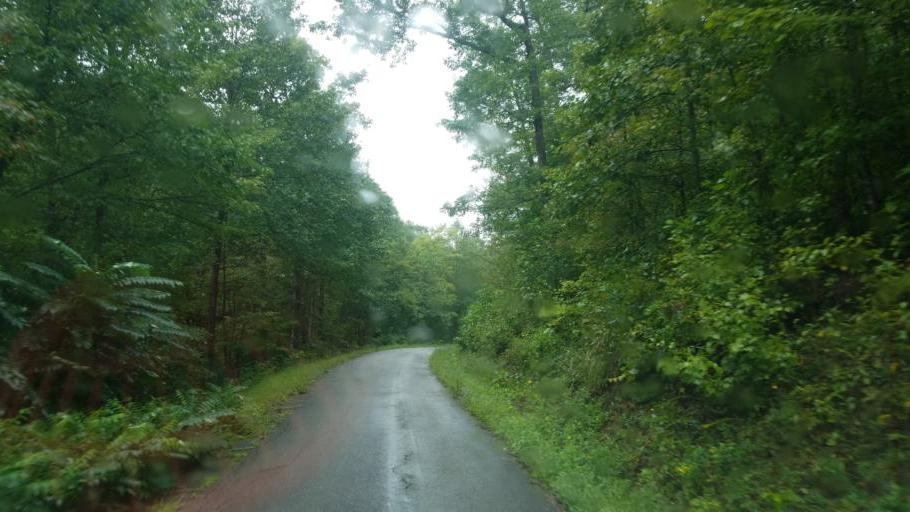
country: US
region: Ohio
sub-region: Scioto County
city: West Portsmouth
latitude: 38.7759
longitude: -83.1566
